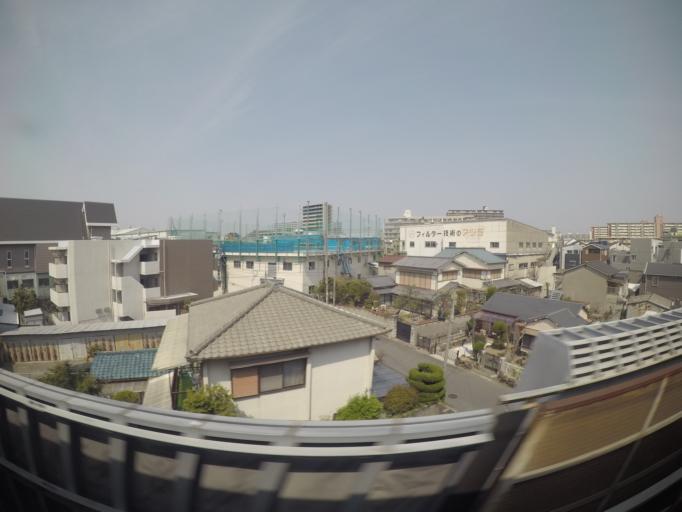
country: JP
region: Osaka
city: Moriguchi
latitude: 34.7530
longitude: 135.5446
